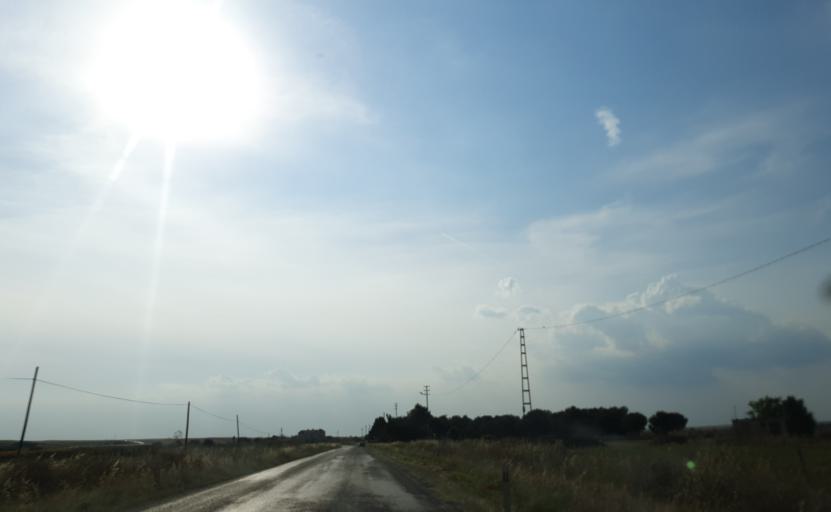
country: TR
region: Tekirdag
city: Muratli
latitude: 41.2158
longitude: 27.4353
